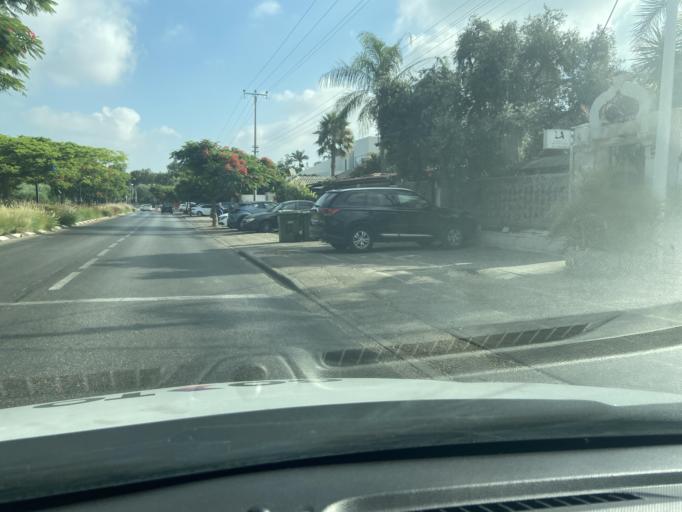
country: IL
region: Central District
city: Yehud
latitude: 32.0390
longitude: 34.8832
